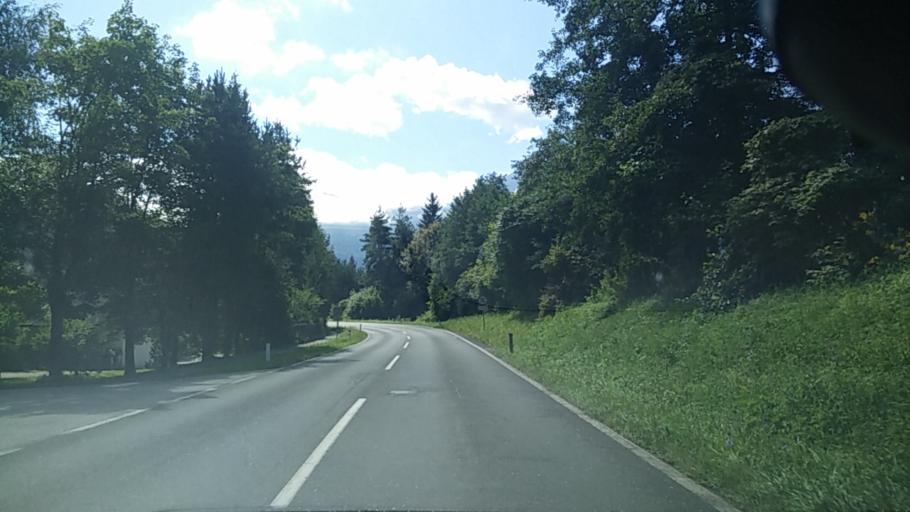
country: AT
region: Carinthia
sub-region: Politischer Bezirk Villach Land
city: Finkenstein am Faaker See
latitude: 46.5731
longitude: 13.8398
